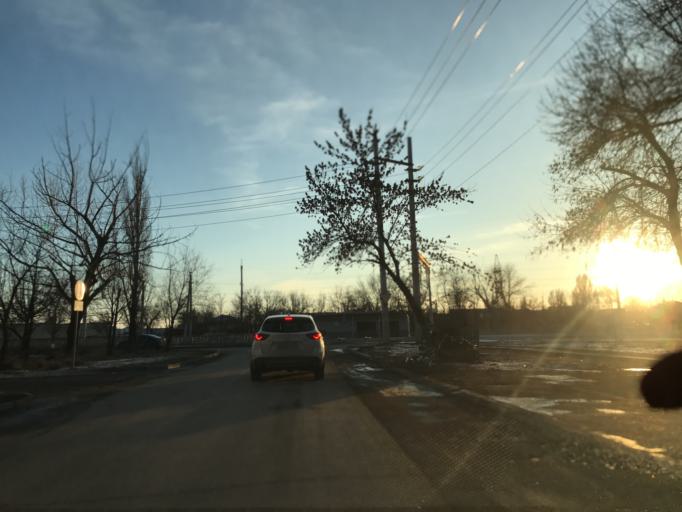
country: RU
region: Rostov
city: Kamensk-Shakhtinskiy
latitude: 48.3160
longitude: 40.2628
